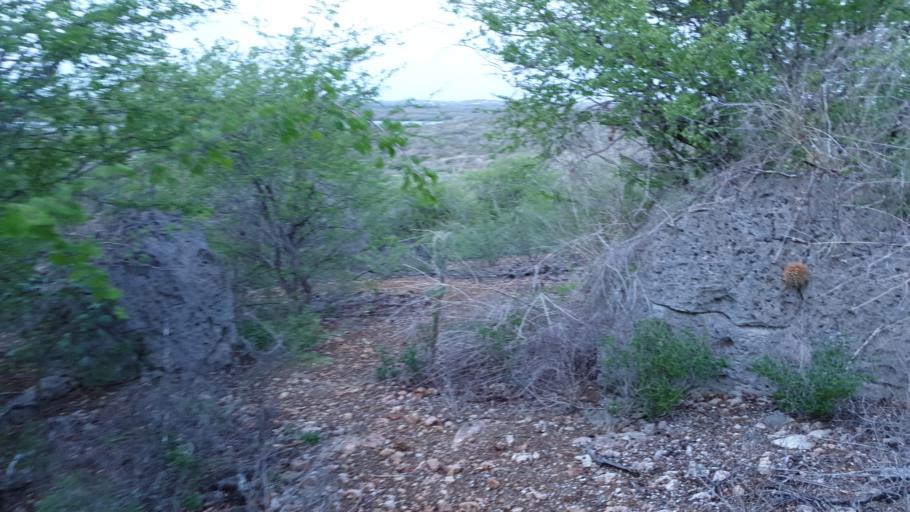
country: CW
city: Newport
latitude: 12.1304
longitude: -68.8148
